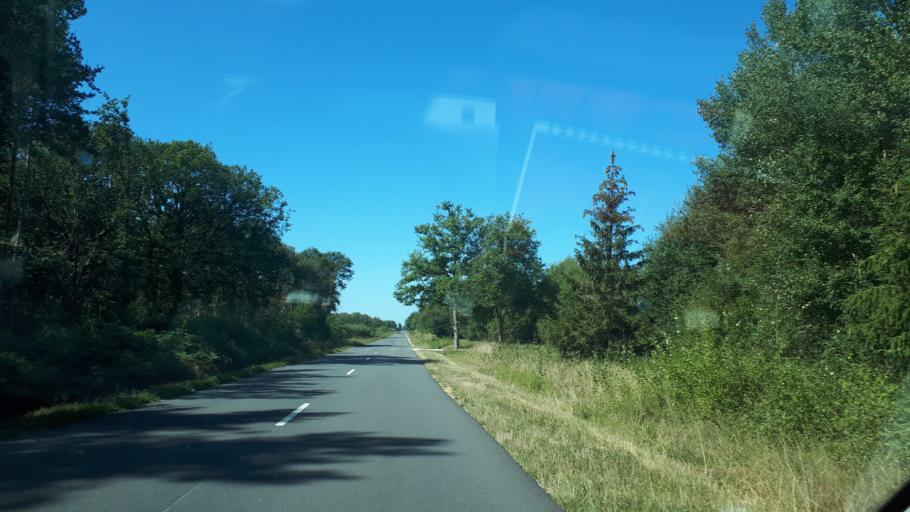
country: FR
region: Centre
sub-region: Departement du Cher
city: Brinon-sur-Sauldre
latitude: 47.6625
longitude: 2.2242
